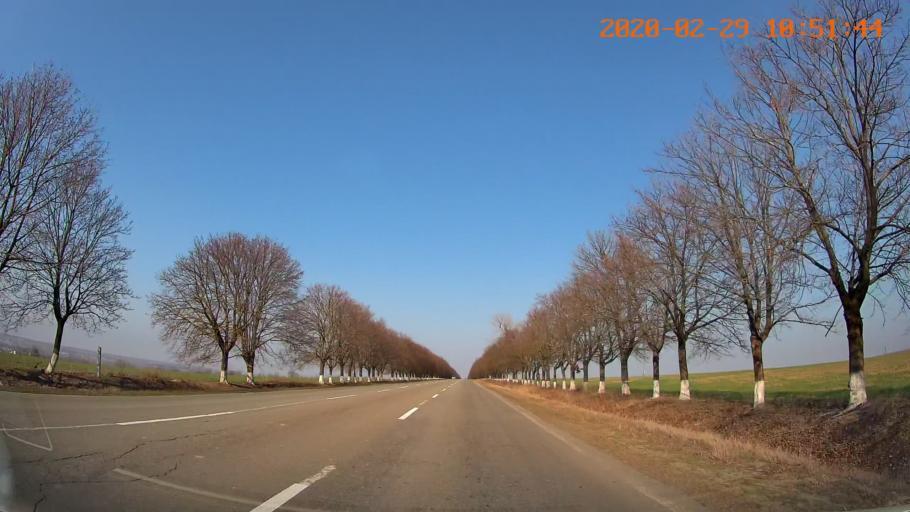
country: MD
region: Telenesti
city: Grigoriopol
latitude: 47.0965
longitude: 29.3603
